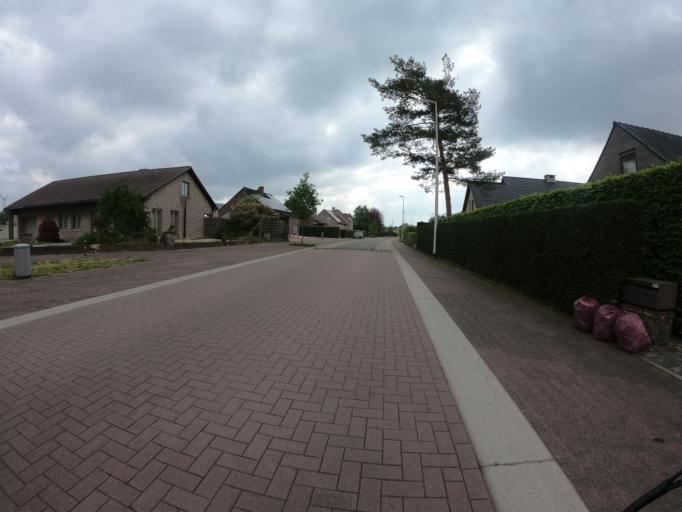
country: BE
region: Flanders
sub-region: Provincie Limburg
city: Genk
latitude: 50.9255
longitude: 5.4743
